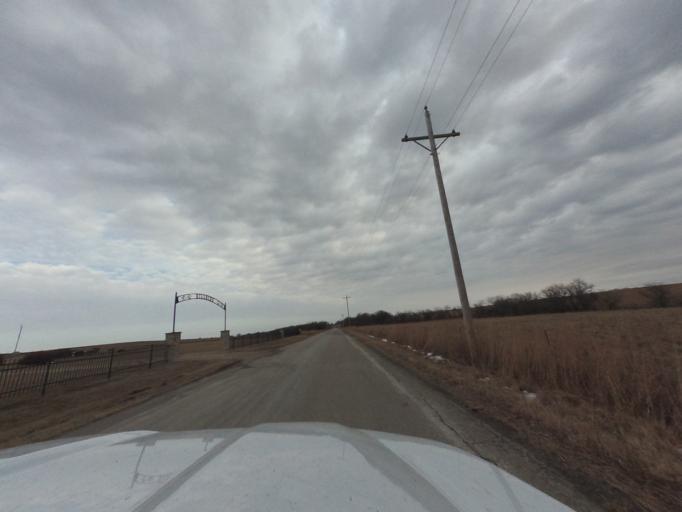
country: US
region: Kansas
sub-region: Chase County
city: Cottonwood Falls
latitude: 38.4300
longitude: -96.3732
